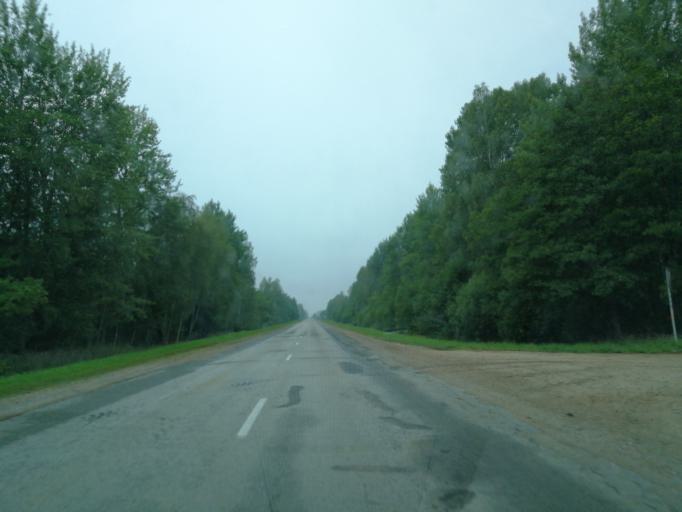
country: LV
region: Varkava
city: Vecvarkava
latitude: 56.3168
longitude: 26.4766
